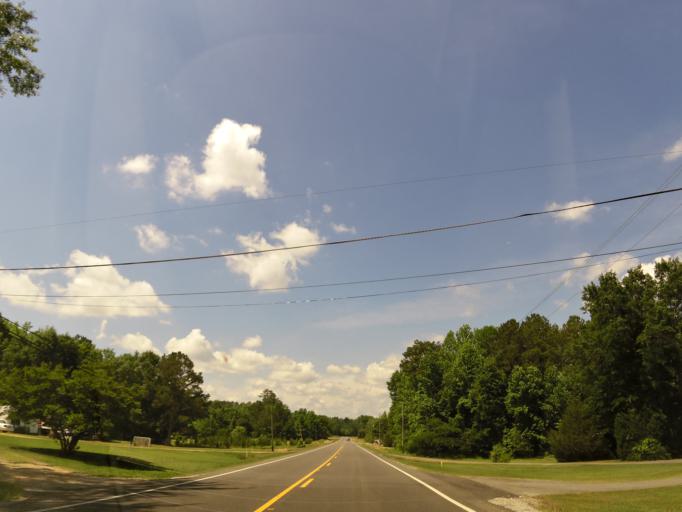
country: US
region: Alabama
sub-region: Marion County
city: Guin
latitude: 33.9299
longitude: -88.0231
